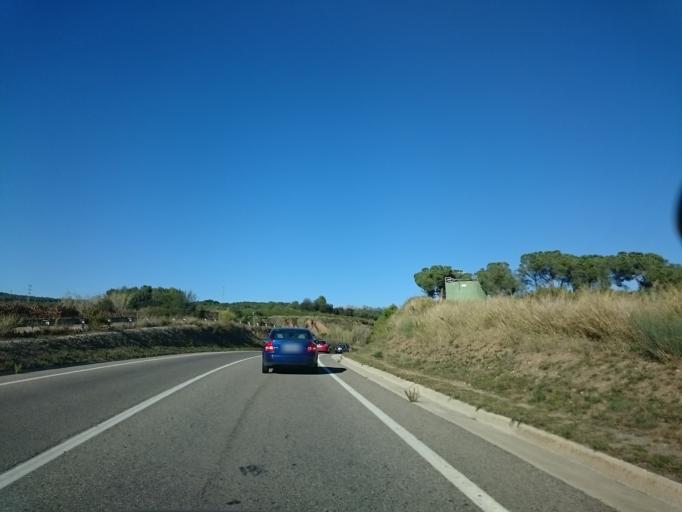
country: ES
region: Catalonia
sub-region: Provincia de Barcelona
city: Piera
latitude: 41.5356
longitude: 1.7309
